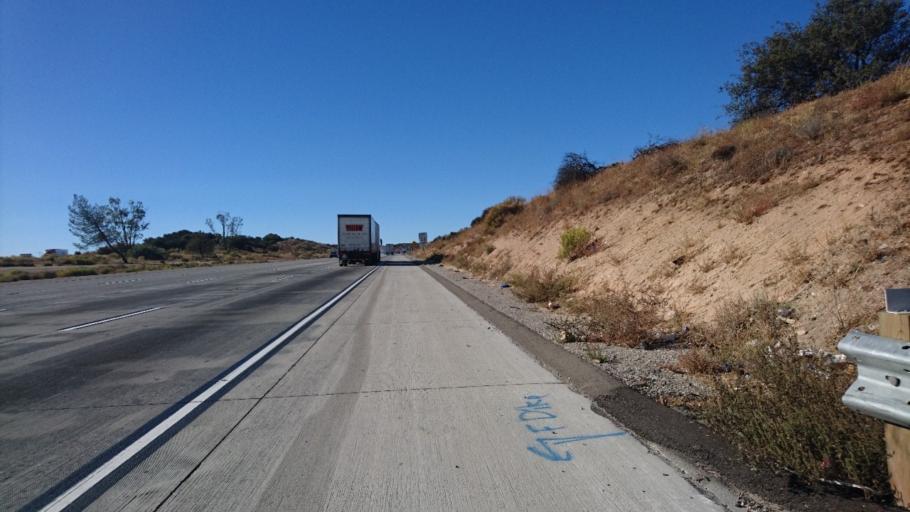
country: US
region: California
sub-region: San Bernardino County
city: Oak Hills
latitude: 34.3576
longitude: -117.4375
